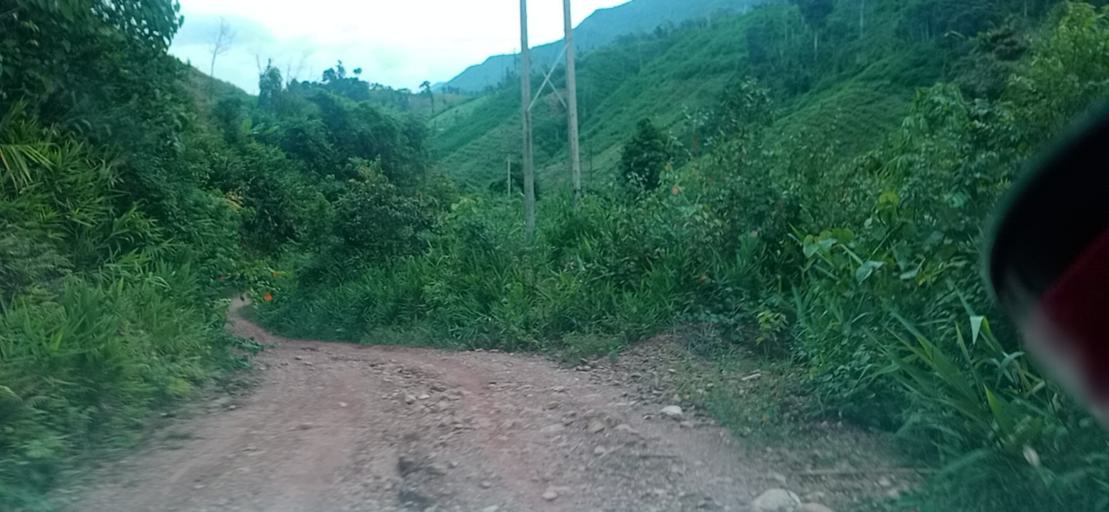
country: TH
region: Changwat Bueng Kan
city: Pak Khat
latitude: 18.5605
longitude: 103.2542
